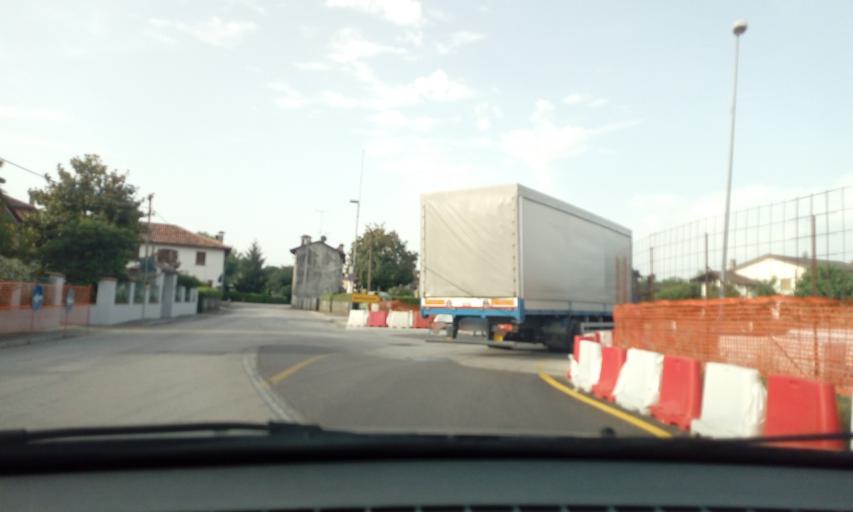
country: IT
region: Friuli Venezia Giulia
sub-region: Provincia di Udine
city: Chiopris
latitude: 45.9279
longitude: 13.3836
